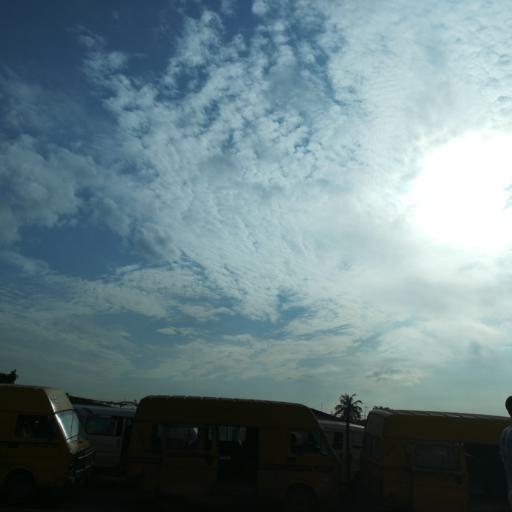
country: NG
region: Lagos
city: Oshodi
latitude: 6.5593
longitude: 3.3503
